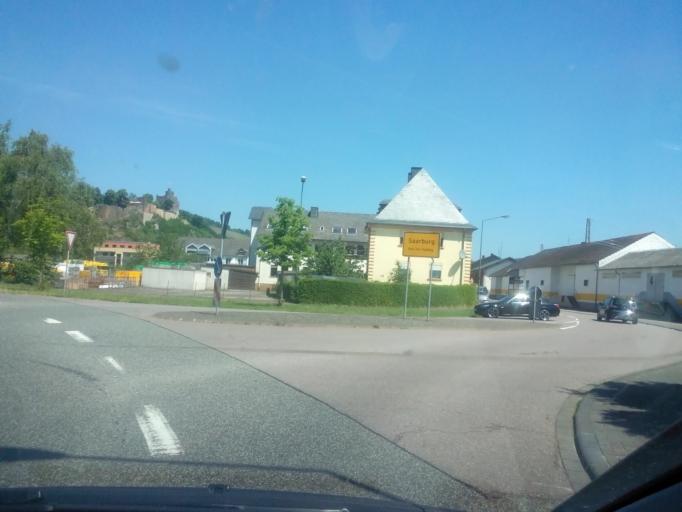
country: DE
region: Rheinland-Pfalz
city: Saarburg
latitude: 49.6049
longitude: 6.5551
